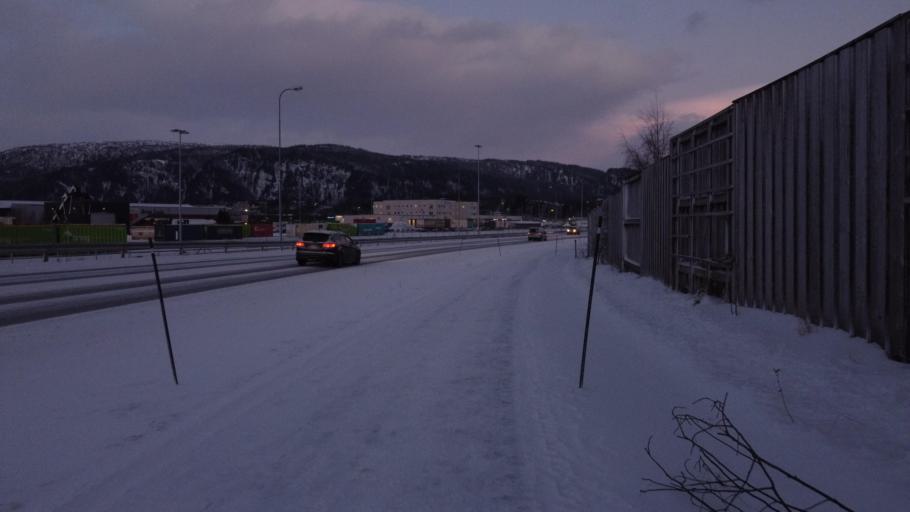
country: NO
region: Nordland
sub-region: Rana
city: Mo i Rana
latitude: 66.3174
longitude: 14.1338
